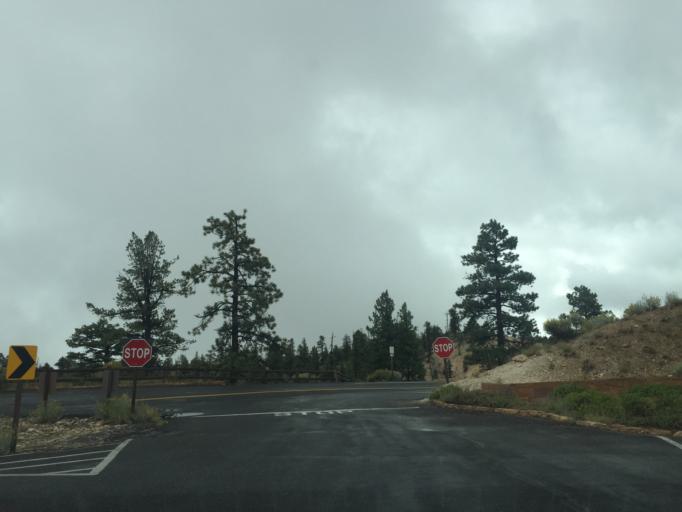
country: US
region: Utah
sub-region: Garfield County
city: Panguitch
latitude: 37.6038
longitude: -112.1567
